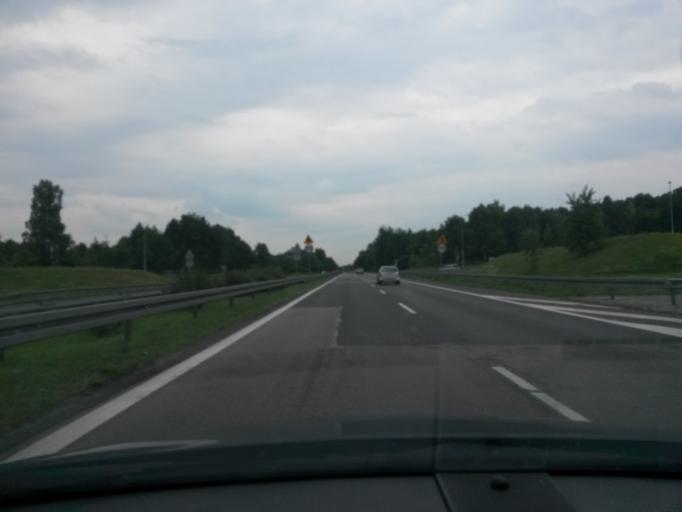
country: PL
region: Silesian Voivodeship
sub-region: Czestochowa
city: Czestochowa
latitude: 50.8475
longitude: 19.1504
